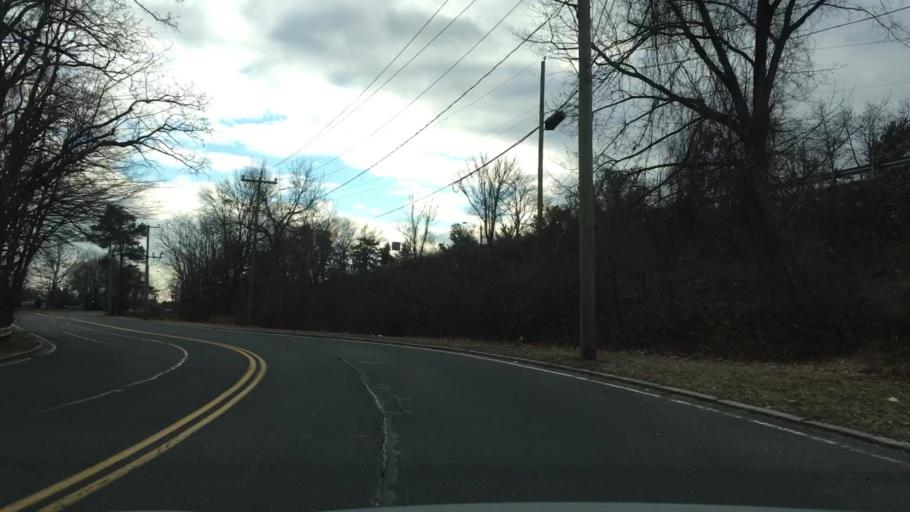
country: US
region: Massachusetts
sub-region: Hampden County
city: Springfield
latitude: 42.1417
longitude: -72.5492
